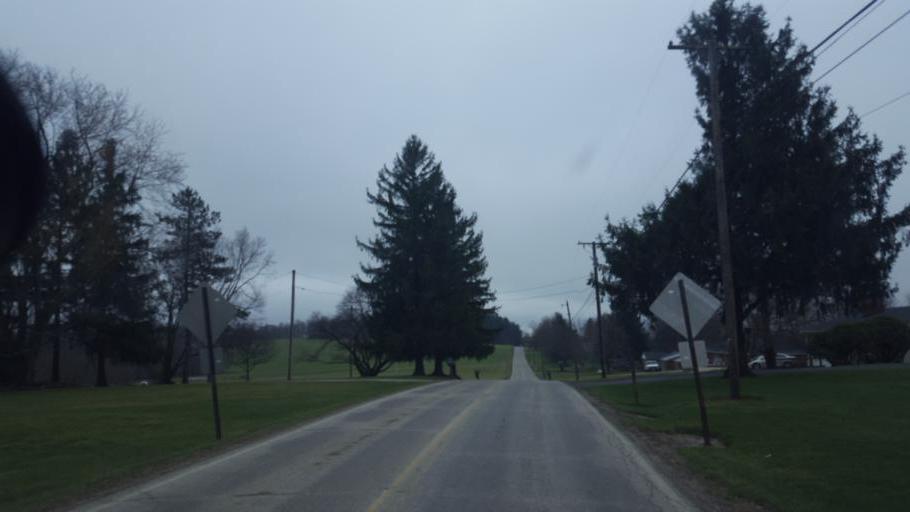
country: US
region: Ohio
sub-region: Richland County
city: Lexington
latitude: 40.6947
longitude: -82.5354
